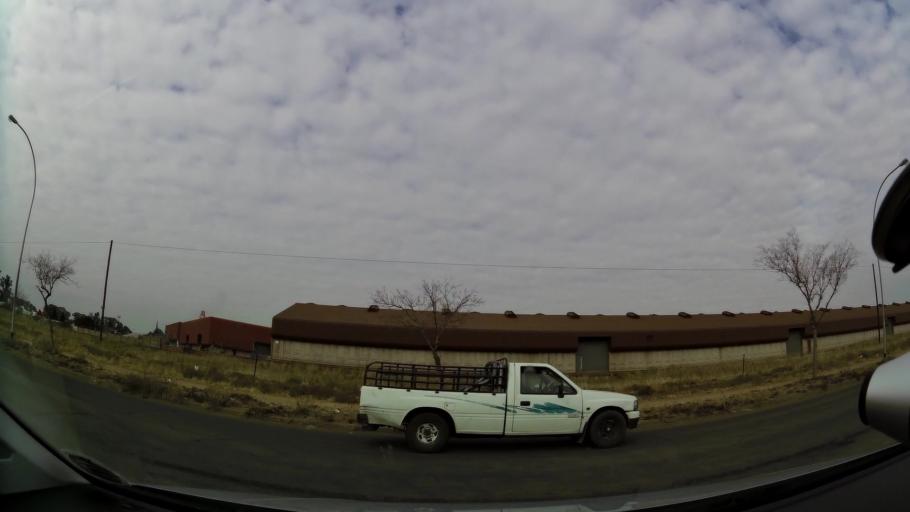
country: ZA
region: Orange Free State
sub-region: Mangaung Metropolitan Municipality
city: Bloemfontein
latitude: -29.1328
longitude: 26.2040
